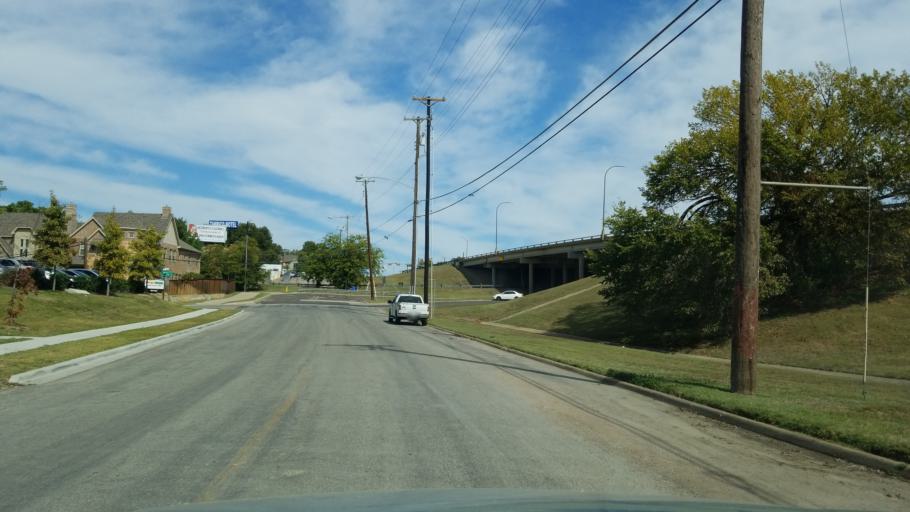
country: US
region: Texas
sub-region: Dallas County
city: Highland Park
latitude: 32.8059
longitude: -96.7343
